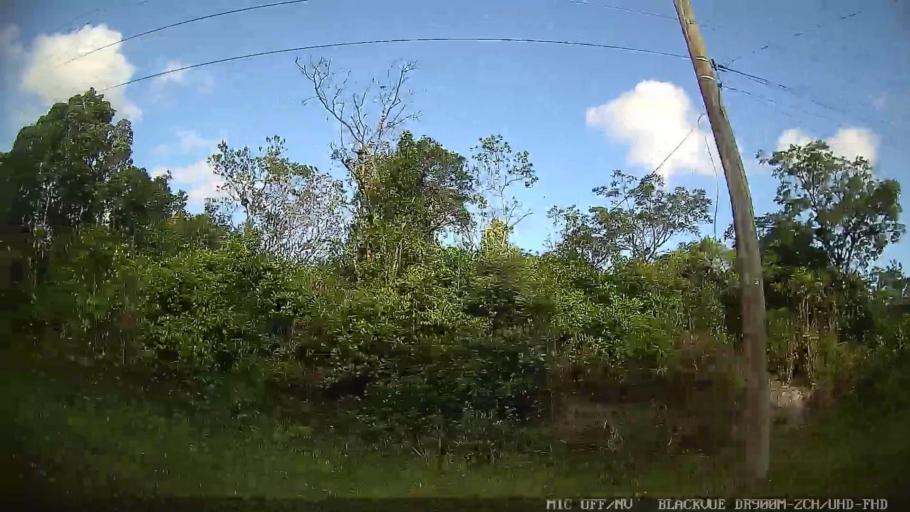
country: BR
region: Sao Paulo
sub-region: Itanhaem
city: Itanhaem
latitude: -24.1483
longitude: -46.8127
